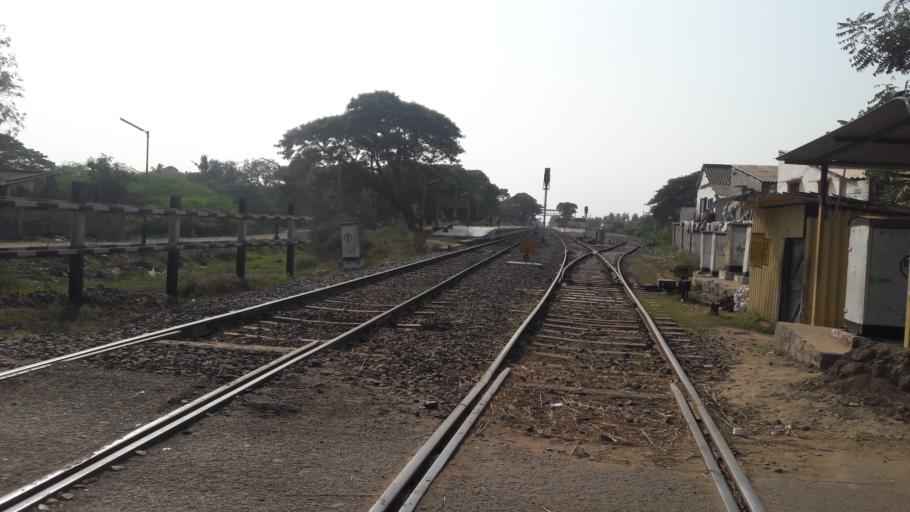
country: IN
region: Andhra Pradesh
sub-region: West Godavari
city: Akividu
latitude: 16.5839
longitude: 81.3722
